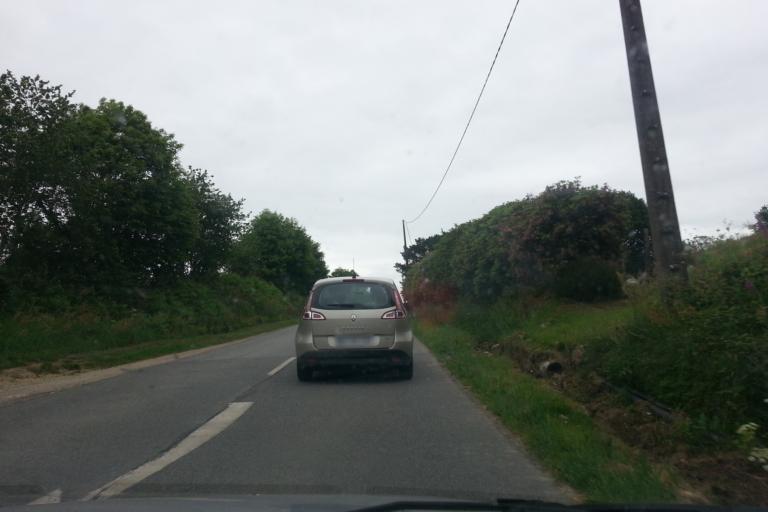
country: FR
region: Brittany
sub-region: Departement du Morbihan
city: Le Faouet
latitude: 48.0519
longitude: -3.4923
